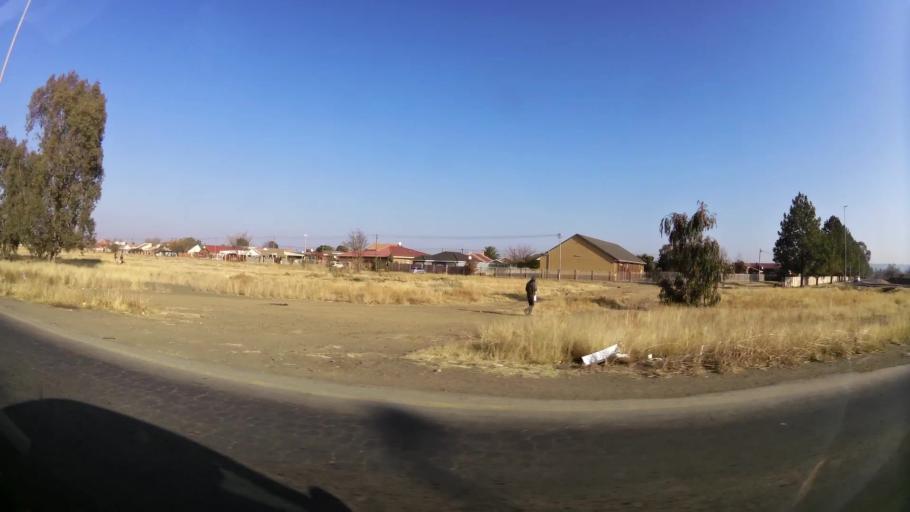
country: ZA
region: Orange Free State
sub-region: Mangaung Metropolitan Municipality
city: Bloemfontein
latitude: -29.1416
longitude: 26.2664
